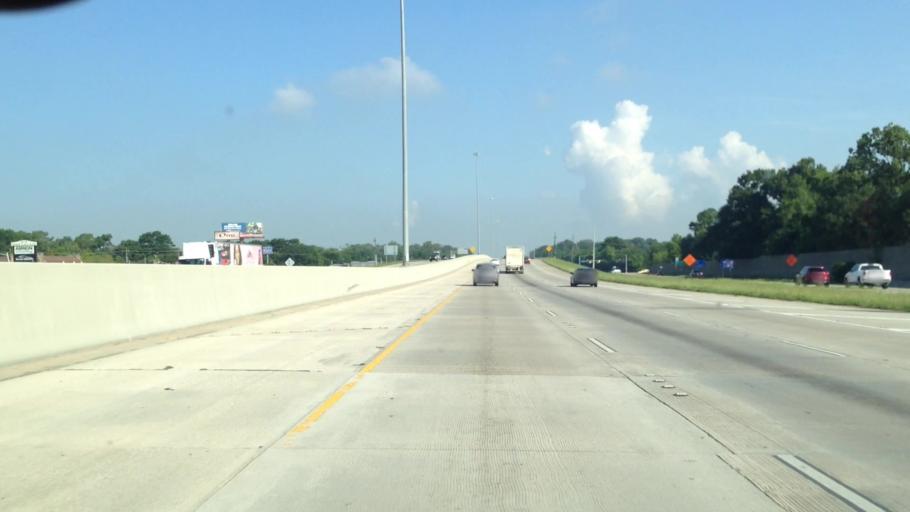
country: US
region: Louisiana
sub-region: East Baton Rouge Parish
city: Westminster
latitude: 30.4051
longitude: -91.0983
